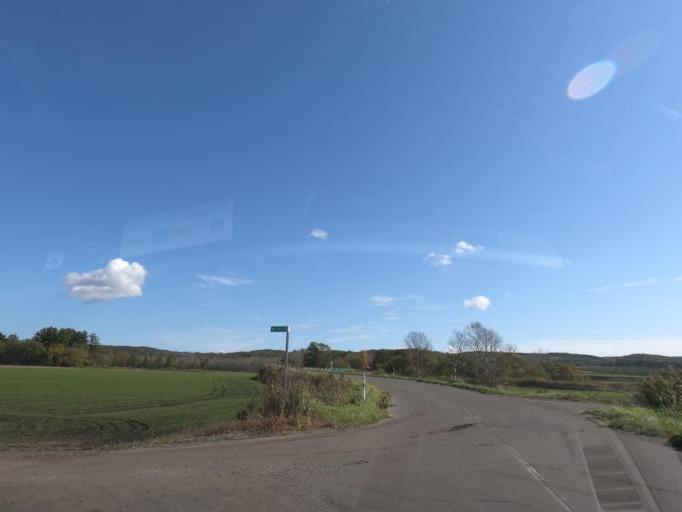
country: JP
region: Hokkaido
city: Otofuke
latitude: 43.0594
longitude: 143.2766
